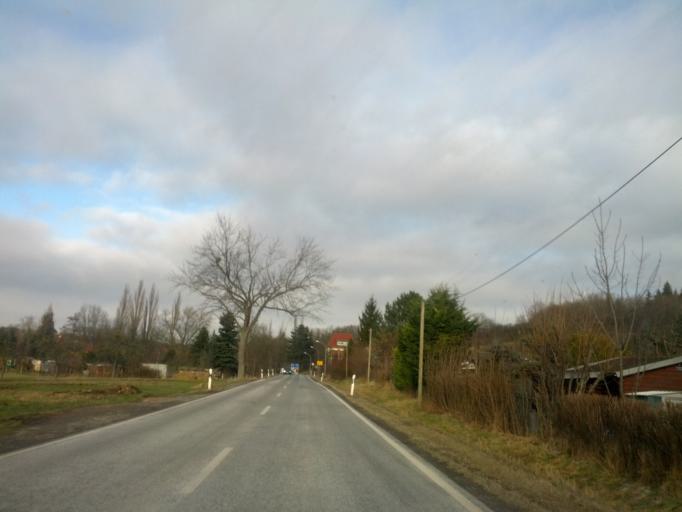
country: DE
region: Thuringia
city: Bad Langensalza
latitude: 51.0953
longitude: 10.6268
